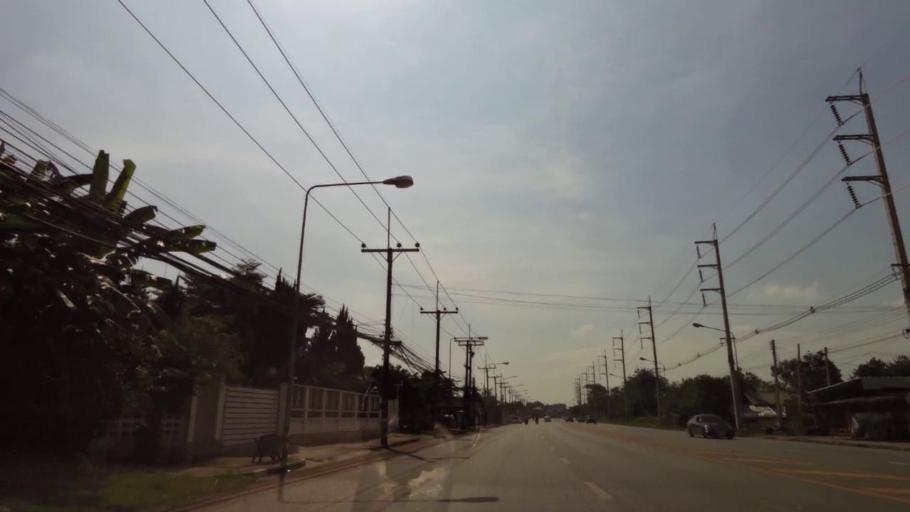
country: TH
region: Chiang Rai
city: Chiang Rai
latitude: 19.8874
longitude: 99.8011
